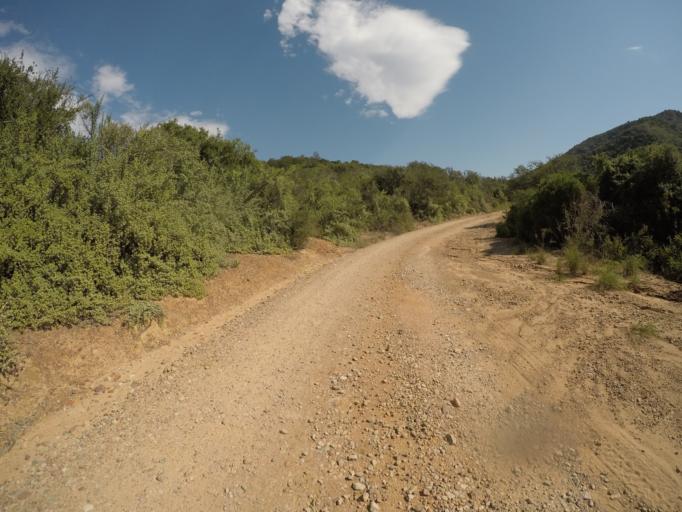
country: ZA
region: Eastern Cape
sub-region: Cacadu District Municipality
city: Kareedouw
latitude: -33.6555
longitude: 24.4083
